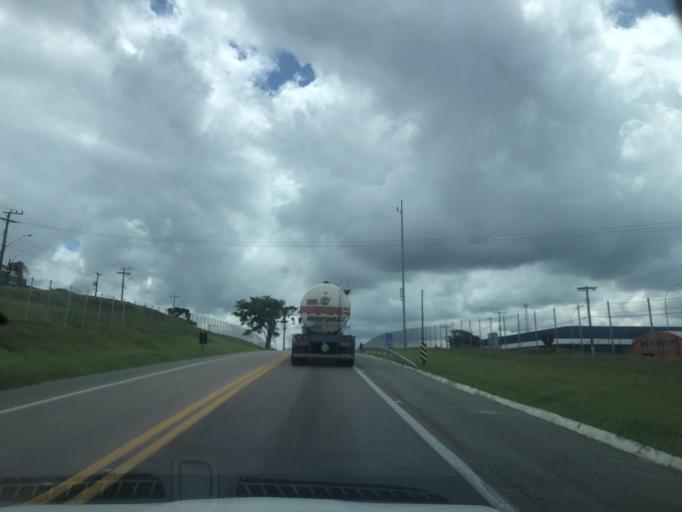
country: BR
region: Parana
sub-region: Rio Negro
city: Rio Negro
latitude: -26.0802
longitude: -49.7700
